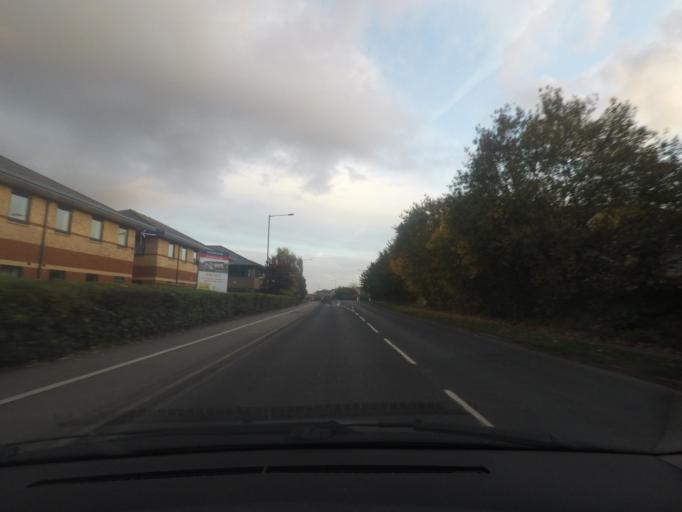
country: GB
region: England
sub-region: City of York
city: Skelton
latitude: 53.9886
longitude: -1.1045
